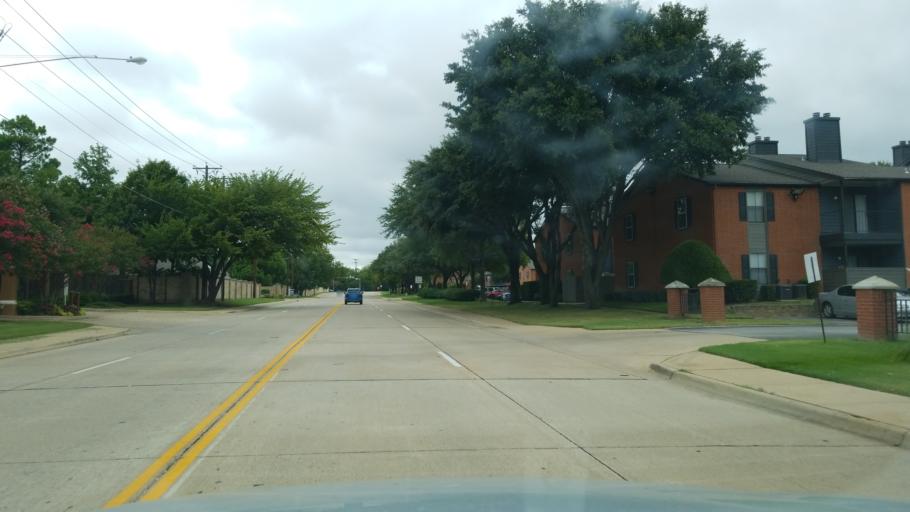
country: US
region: Texas
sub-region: Tarrant County
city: Bedford
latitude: 32.8425
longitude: -97.1227
